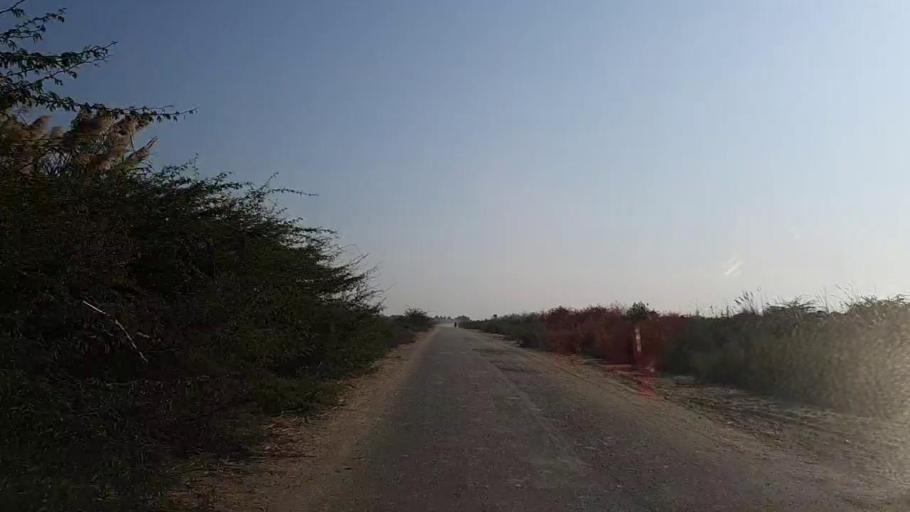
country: PK
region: Sindh
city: Tando Mittha Khan
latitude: 25.9101
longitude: 69.0761
